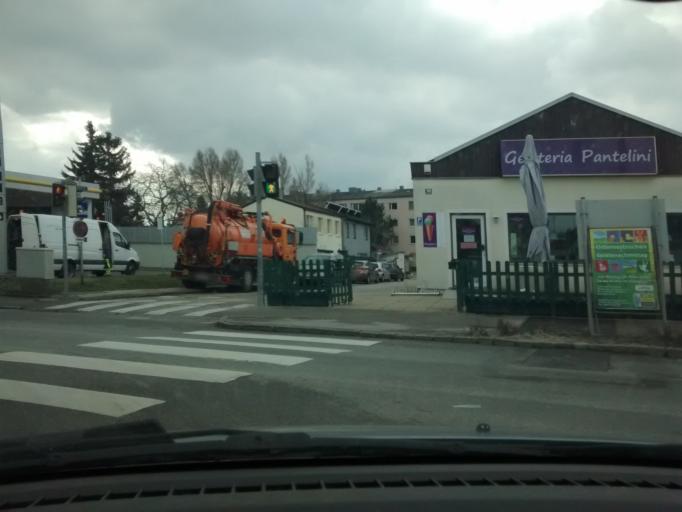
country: AT
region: Lower Austria
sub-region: Politischer Bezirk Modling
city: Wiener Neudorf
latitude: 48.0865
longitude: 16.3177
